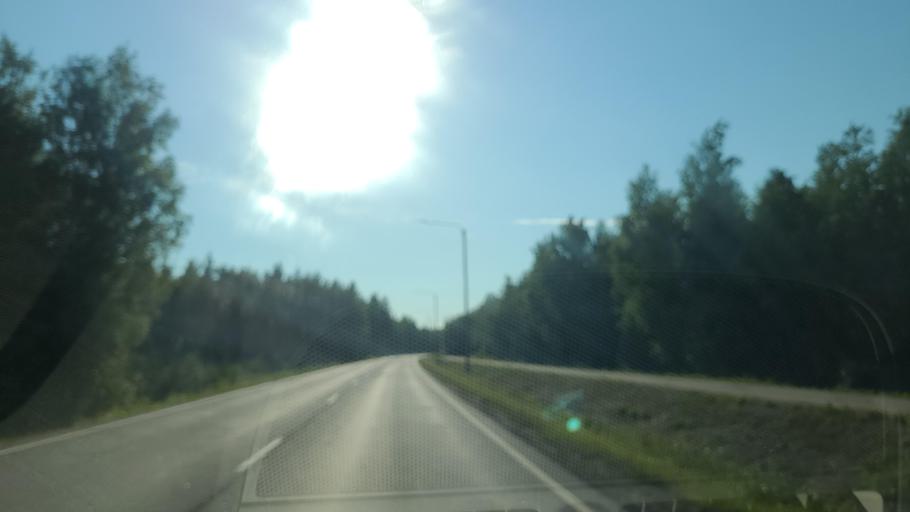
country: FI
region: Ostrobothnia
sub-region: Vaasa
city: Replot
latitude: 63.2070
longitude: 21.4501
